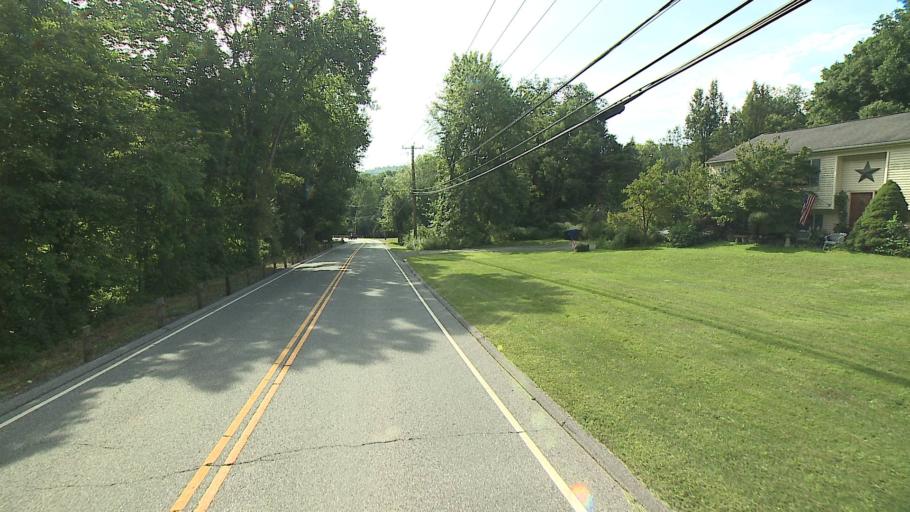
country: US
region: Connecticut
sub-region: Fairfield County
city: Sherman
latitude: 41.5916
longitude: -73.4690
